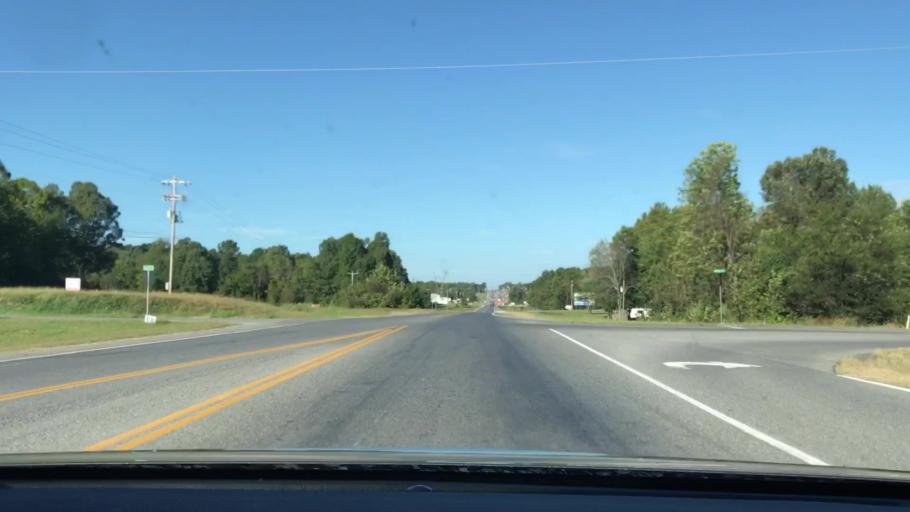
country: US
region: Kentucky
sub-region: Marshall County
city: Calvert City
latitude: 37.0032
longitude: -88.3301
